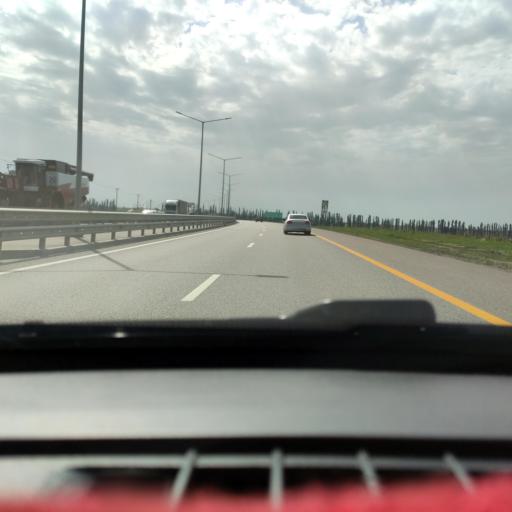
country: RU
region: Voronezj
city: Kashirskoye
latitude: 51.4866
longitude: 39.5341
